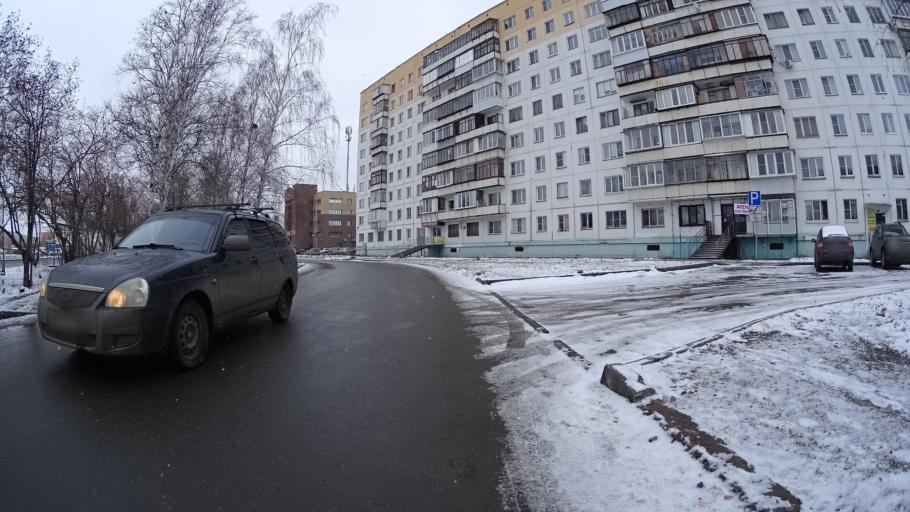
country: RU
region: Chelyabinsk
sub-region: Gorod Chelyabinsk
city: Chelyabinsk
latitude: 55.1907
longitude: 61.3216
